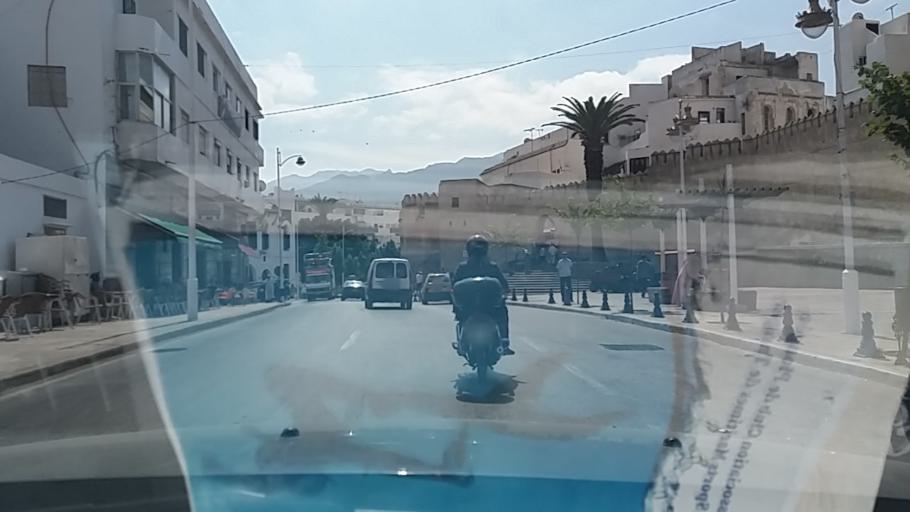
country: MA
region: Tanger-Tetouan
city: Tetouan
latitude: 35.5711
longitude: -5.3635
